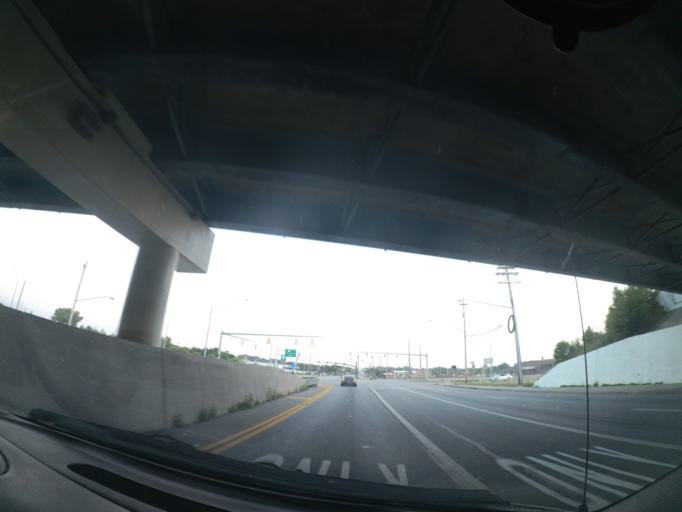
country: US
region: Ohio
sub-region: Lake County
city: Mentor
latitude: 41.6864
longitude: -81.3394
